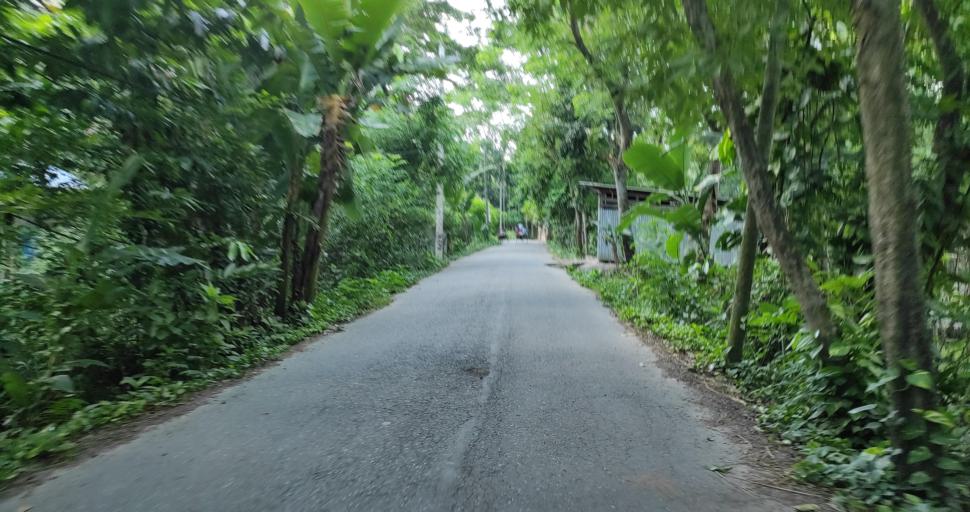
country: BD
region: Barisal
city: Gaurnadi
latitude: 22.8963
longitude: 90.1839
